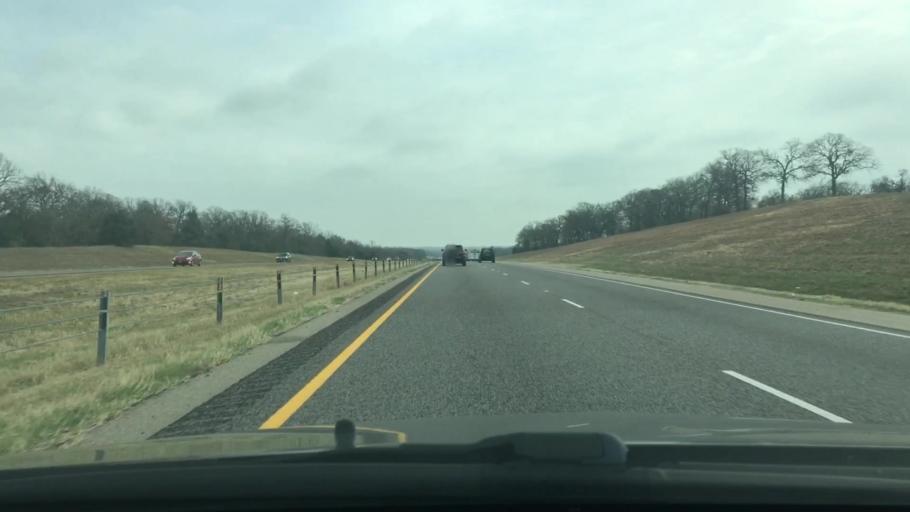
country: US
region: Texas
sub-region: Leon County
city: Buffalo
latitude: 31.5307
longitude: -96.1167
